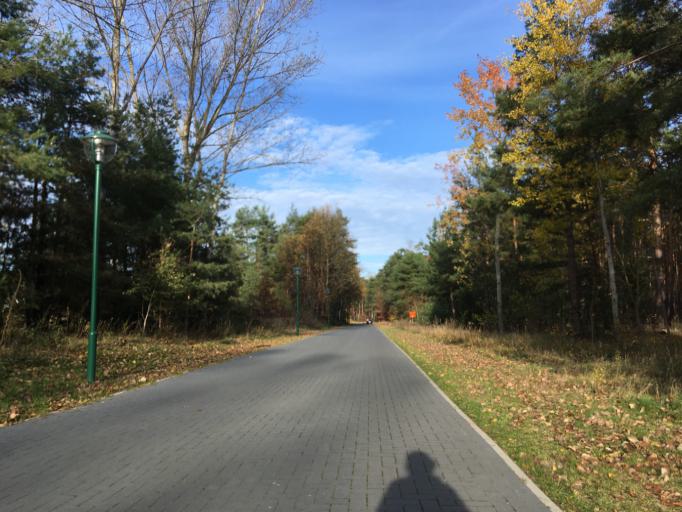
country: DE
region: Brandenburg
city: Halbe
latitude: 52.1119
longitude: 13.7029
